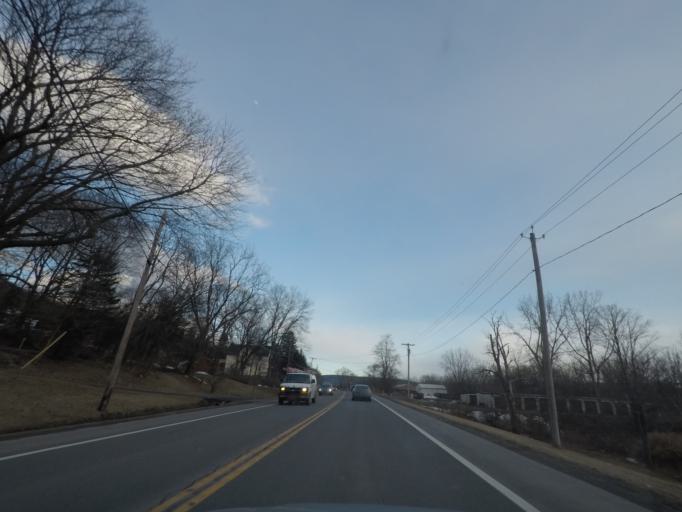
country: US
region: New York
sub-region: Herkimer County
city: Ilion
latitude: 43.0268
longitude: -75.0405
